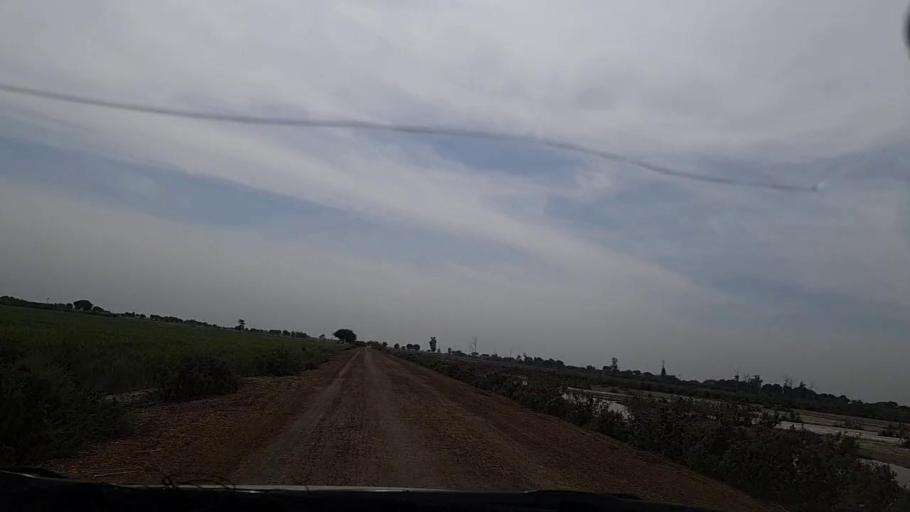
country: PK
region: Sindh
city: Dhoro Naro
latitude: 25.4473
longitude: 69.4922
